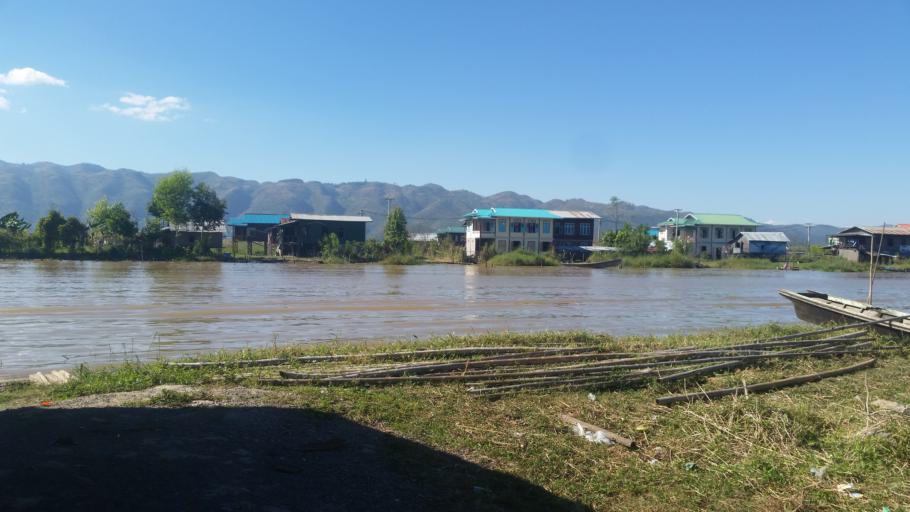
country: MM
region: Shan
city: Taunggyi
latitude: 20.6420
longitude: 96.9220
